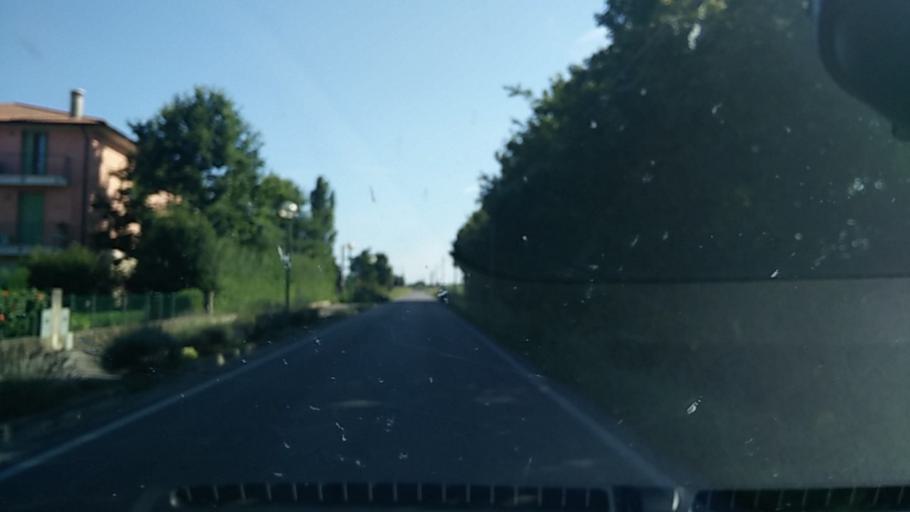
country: IT
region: Veneto
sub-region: Provincia di Treviso
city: Monastier di Treviso
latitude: 45.6776
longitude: 12.4036
